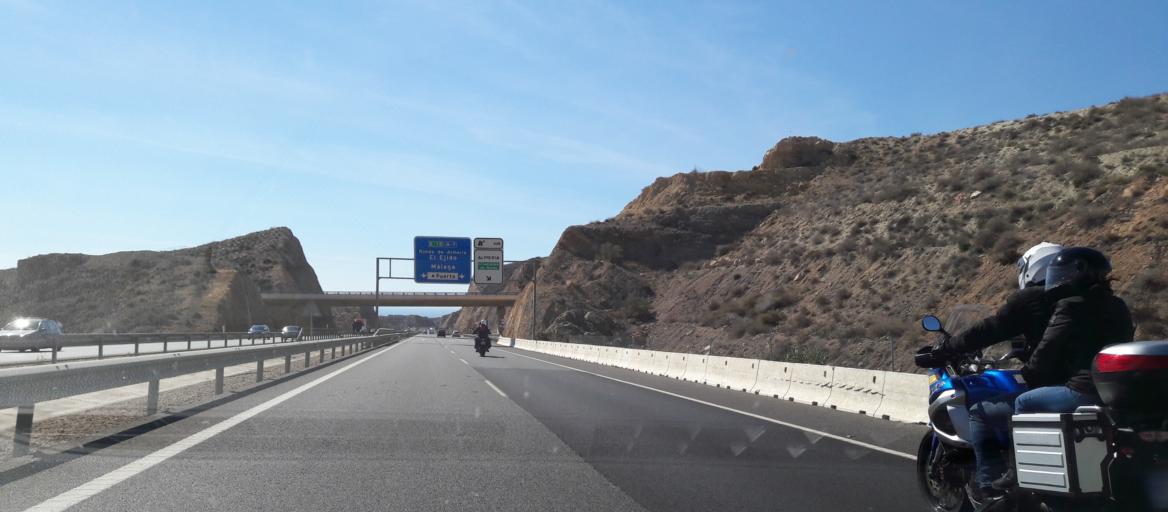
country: ES
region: Andalusia
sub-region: Provincia de Almeria
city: Huercal de Almeria
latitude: 36.8758
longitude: -2.4600
